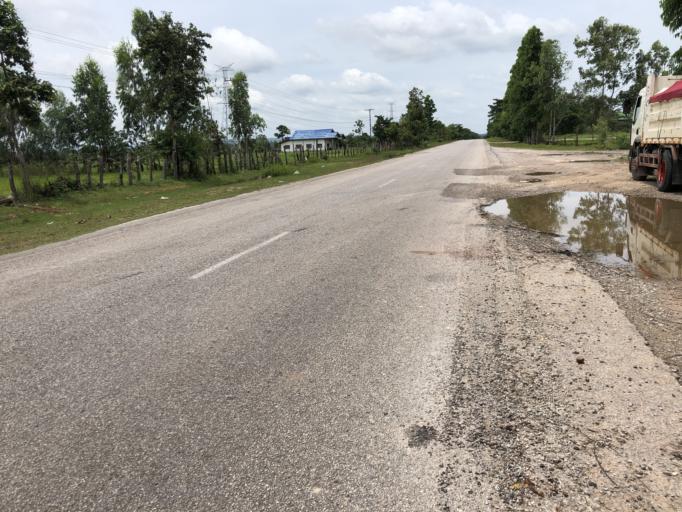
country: TH
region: Nakhon Phanom
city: That Phanom
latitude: 17.0431
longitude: 104.9951
